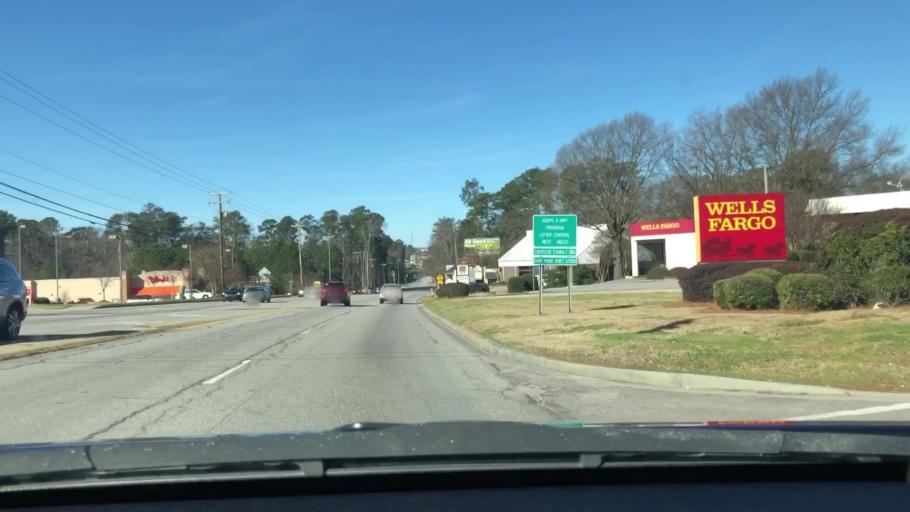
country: US
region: South Carolina
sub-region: Lexington County
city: Oak Grove
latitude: 34.0048
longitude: -81.1162
